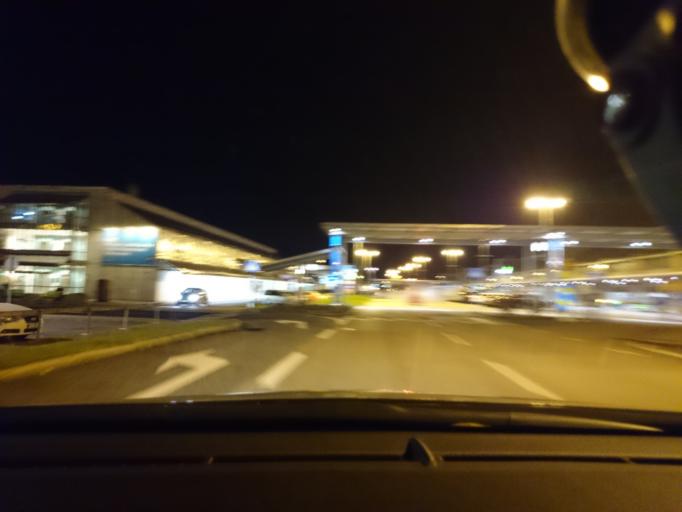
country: SE
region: Vaestra Goetaland
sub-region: Harryda Kommun
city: Landvetter
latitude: 57.6692
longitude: 12.2974
